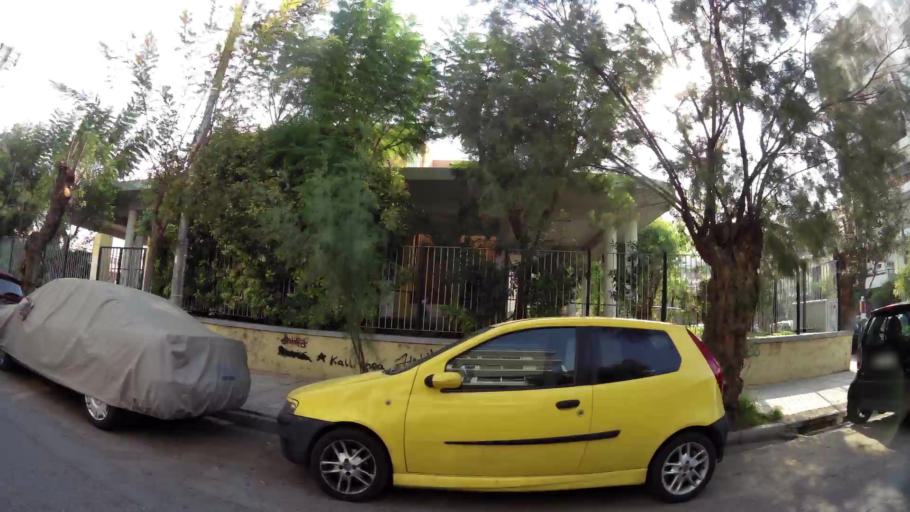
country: GR
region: Attica
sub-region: Nomarchia Athinas
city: Moskhaton
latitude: 37.9462
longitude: 23.6847
